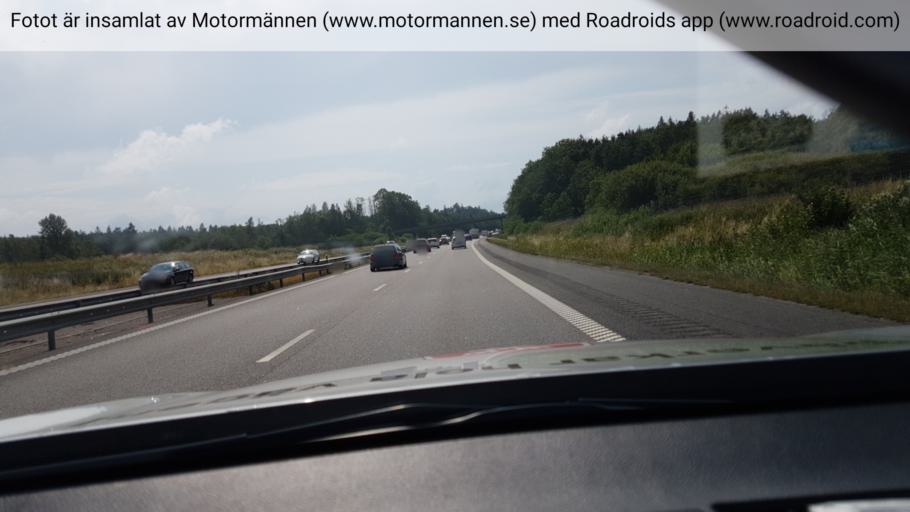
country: SE
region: Halland
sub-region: Kungsbacka Kommun
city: Kungsbacka
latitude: 57.5037
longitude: 12.0527
